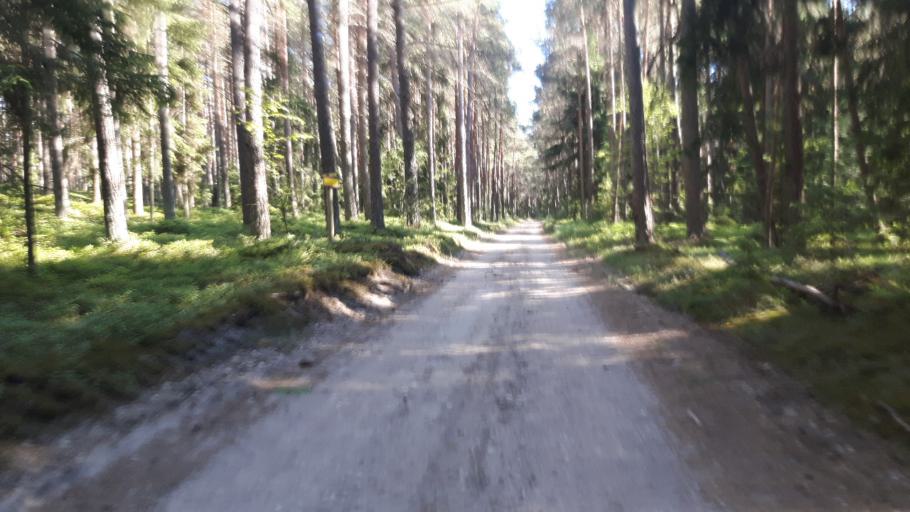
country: LV
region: Salacgrivas
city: Salacgriva
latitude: 57.7323
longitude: 24.3500
